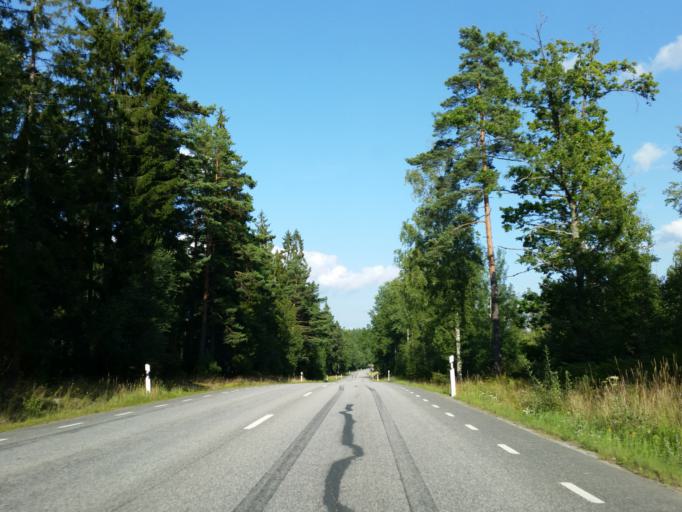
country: SE
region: Stockholm
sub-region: Nykvarns Kommun
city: Nykvarn
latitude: 59.2085
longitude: 17.3438
